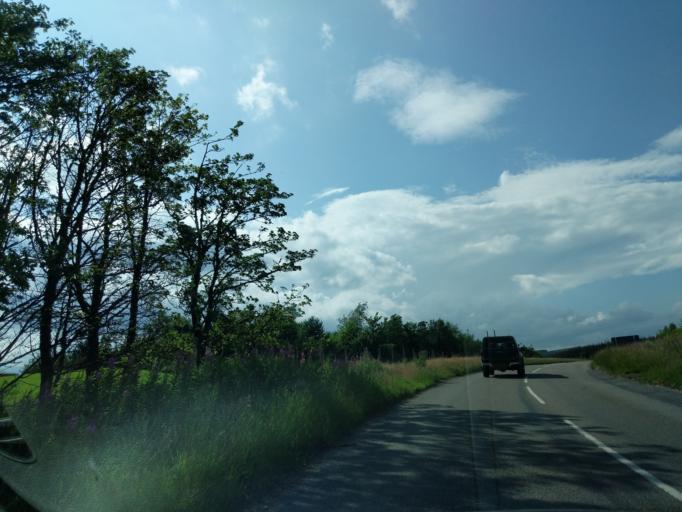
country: GB
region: Scotland
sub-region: Moray
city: Rothes
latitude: 57.4902
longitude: -3.2073
